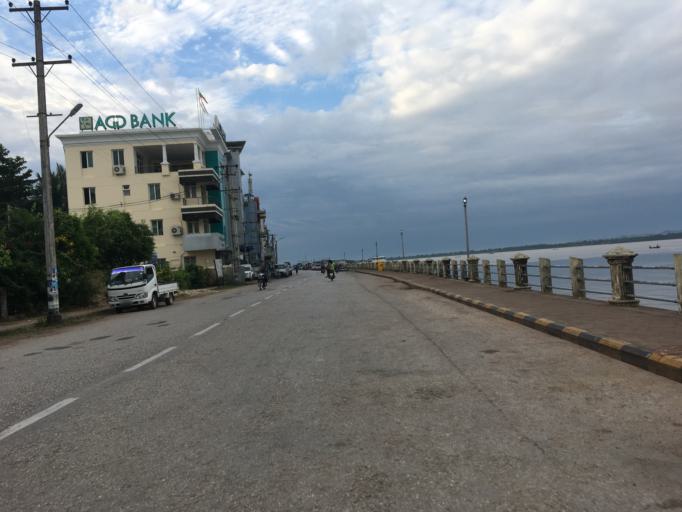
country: MM
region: Mon
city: Mawlamyine
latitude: 16.4974
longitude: 97.6181
